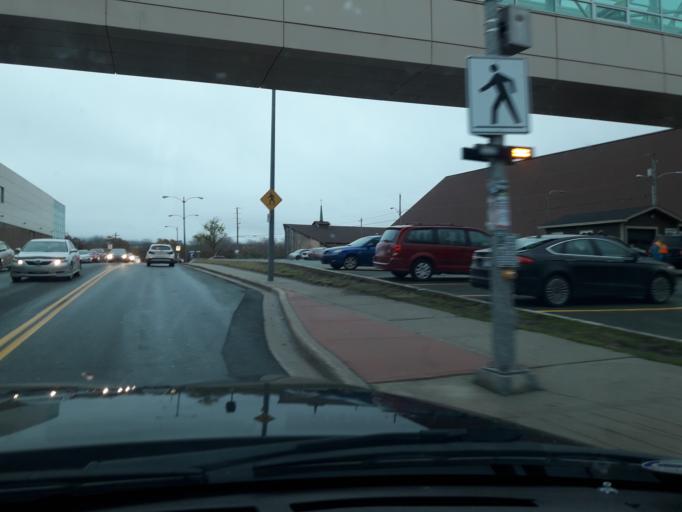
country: CA
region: Newfoundland and Labrador
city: St. John's
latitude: 47.5700
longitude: -52.7358
